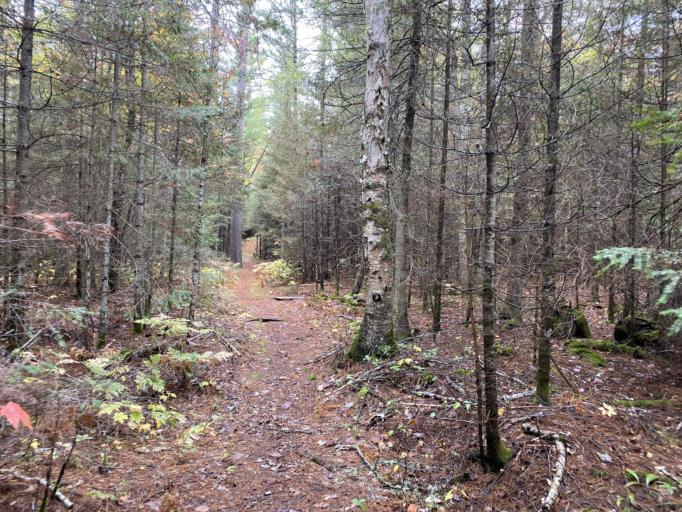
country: US
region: Michigan
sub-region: Marquette County
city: West Ishpeming
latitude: 46.5354
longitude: -88.0016
